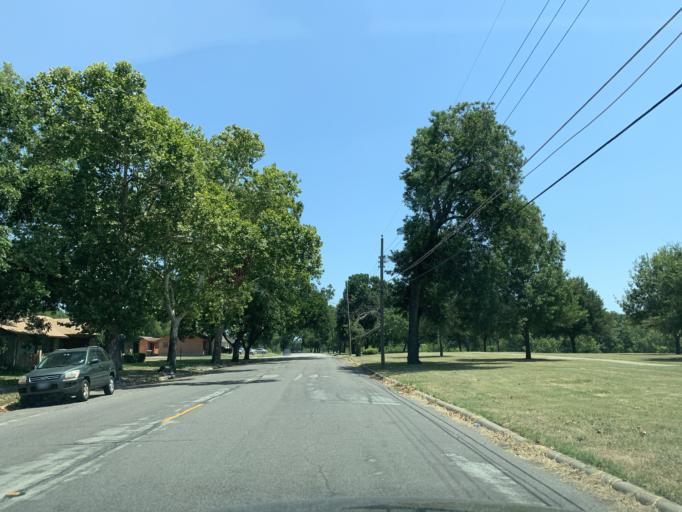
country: US
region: Texas
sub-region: Dallas County
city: Cockrell Hill
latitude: 32.6847
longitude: -96.8054
